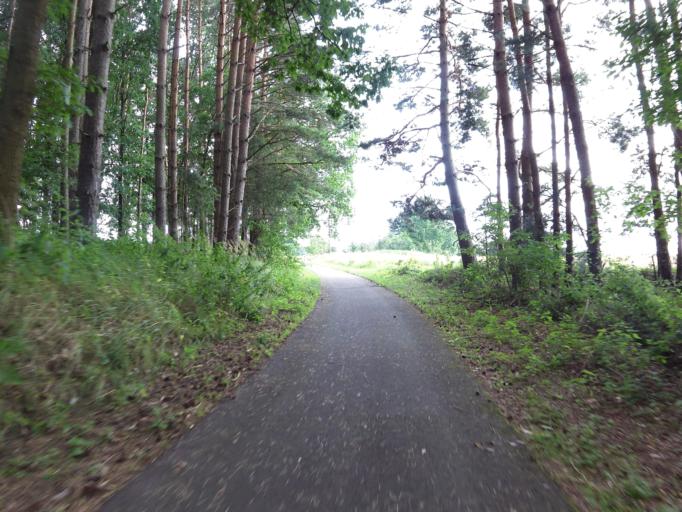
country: DE
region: Brandenburg
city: Lychen
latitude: 53.2599
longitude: 13.3093
